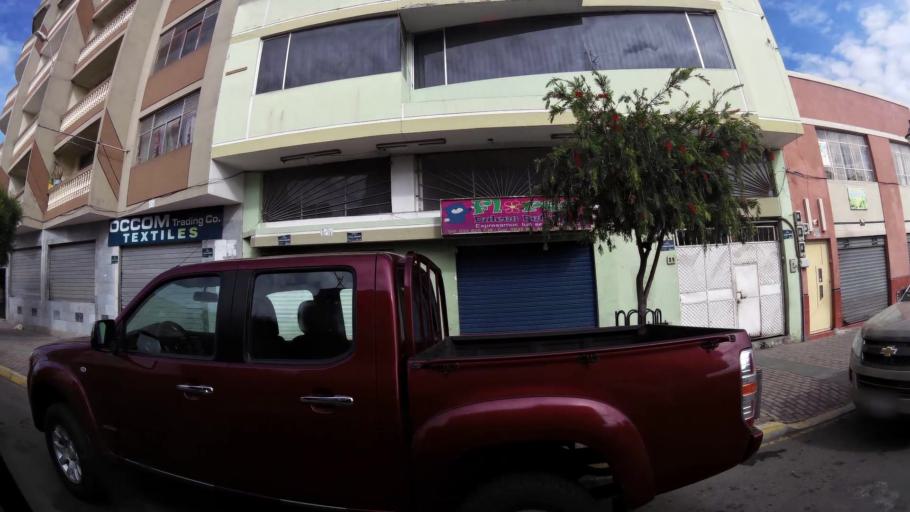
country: EC
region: Tungurahua
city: Ambato
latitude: -1.2522
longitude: -78.6446
